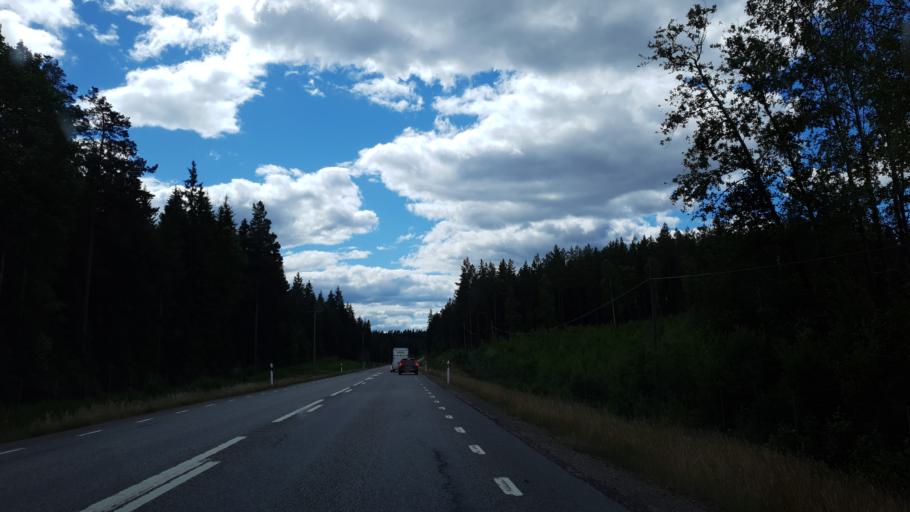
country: SE
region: Kronoberg
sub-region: Vaxjo Kommun
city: Braas
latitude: 57.1791
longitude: 15.1587
